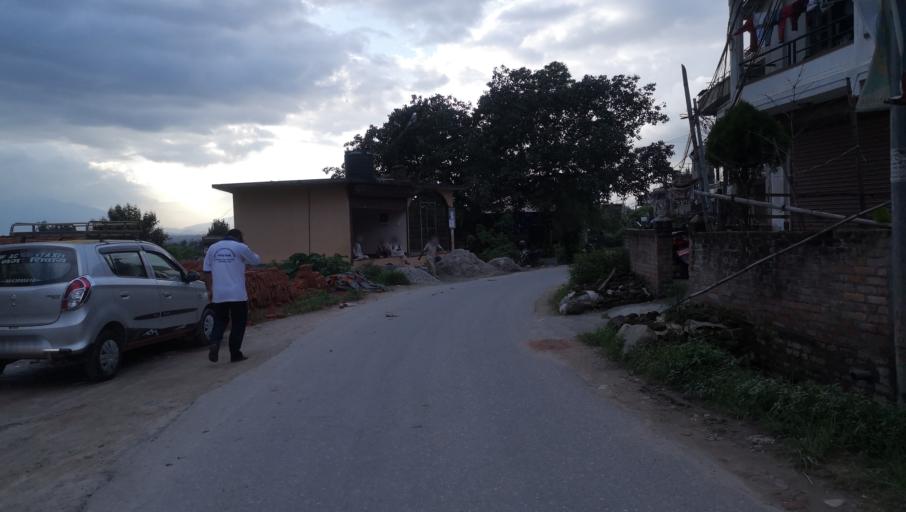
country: NP
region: Central Region
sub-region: Bagmati Zone
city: Bhaktapur
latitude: 27.6486
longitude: 85.3860
